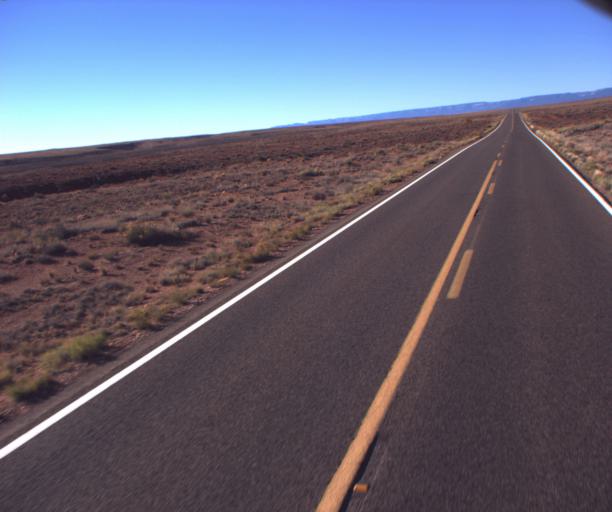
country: US
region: Arizona
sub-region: Coconino County
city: Page
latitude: 36.7308
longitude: -111.7598
